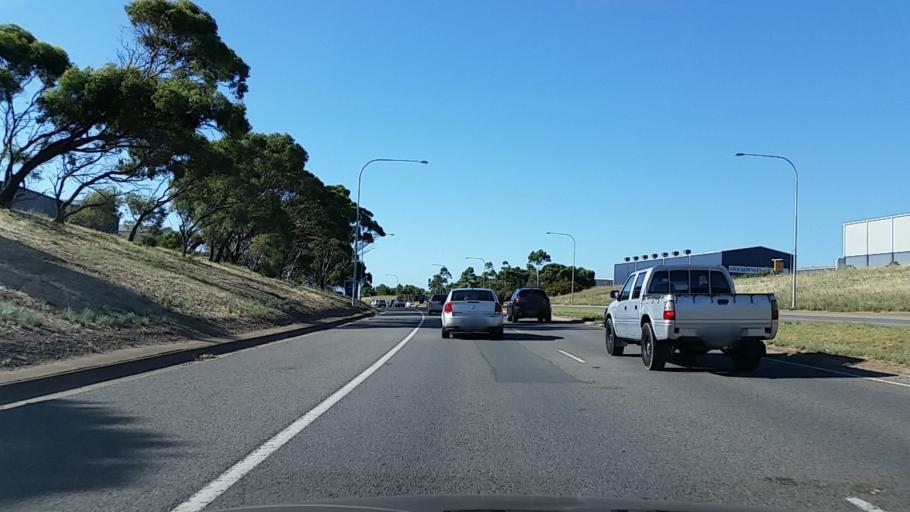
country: AU
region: South Australia
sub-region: Onkaparinga
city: Reynella
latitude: -35.1040
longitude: 138.4998
